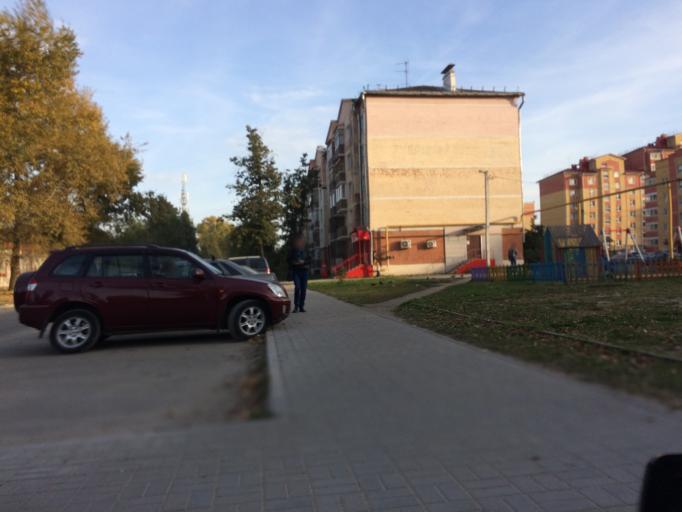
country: RU
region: Mariy-El
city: Yoshkar-Ola
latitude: 56.6307
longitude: 47.8516
